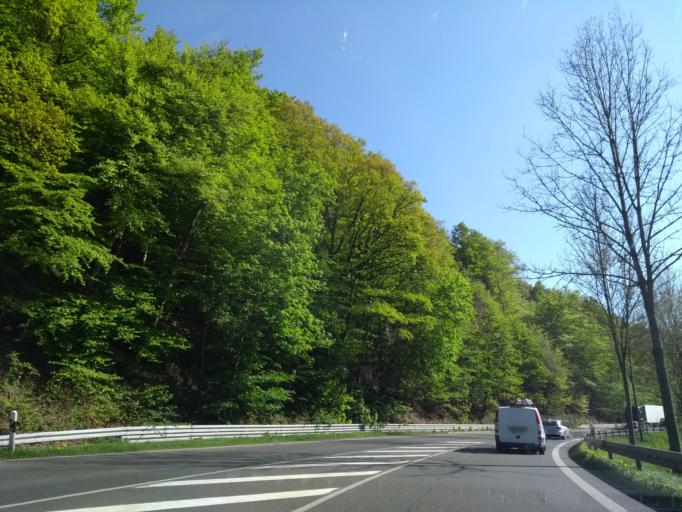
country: DE
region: Hesse
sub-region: Regierungsbezirk Kassel
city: Vohl
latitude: 51.2128
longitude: 8.8988
